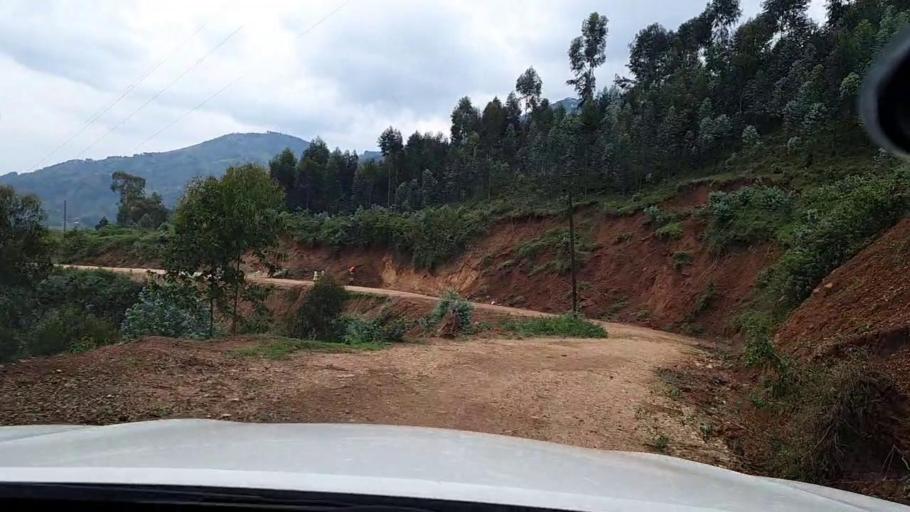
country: RW
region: Western Province
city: Kibuye
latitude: -2.2832
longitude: 29.3031
